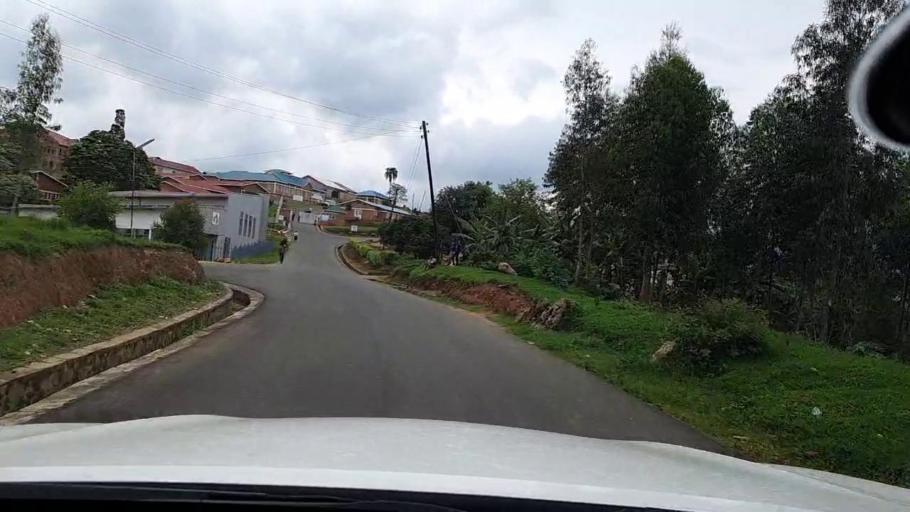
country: RW
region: Western Province
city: Kibuye
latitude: -2.1797
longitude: 29.2908
